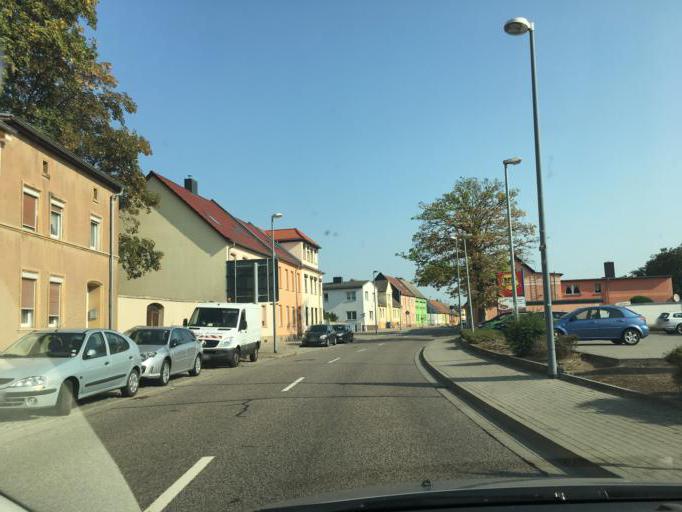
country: DE
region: Saxony-Anhalt
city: Nienburg/Saale
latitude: 51.8371
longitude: 11.7661
